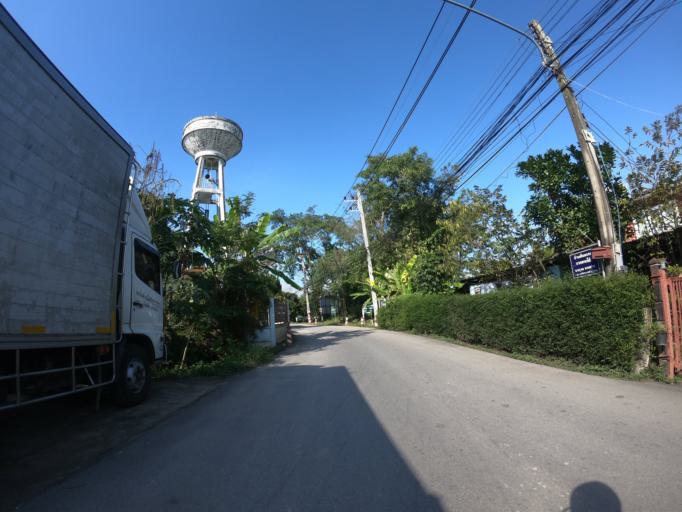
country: TH
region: Chiang Mai
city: Saraphi
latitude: 18.7153
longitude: 99.0040
